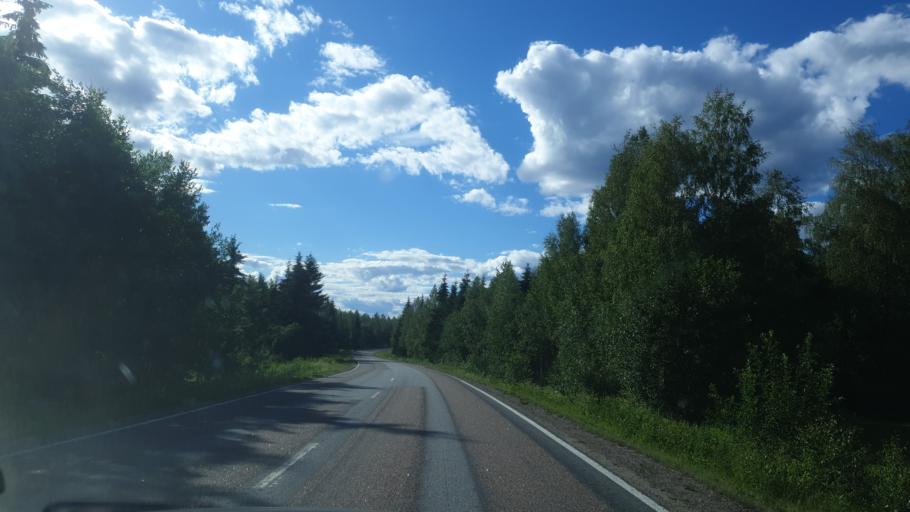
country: FI
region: Southern Savonia
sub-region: Mikkeli
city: Maentyharju
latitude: 61.4829
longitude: 26.7410
